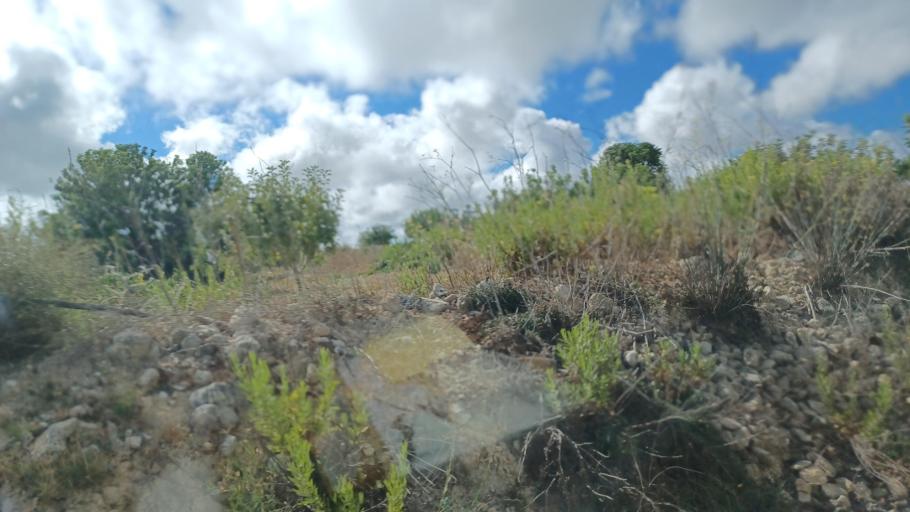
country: CY
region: Pafos
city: Tala
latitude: 34.8559
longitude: 32.4474
